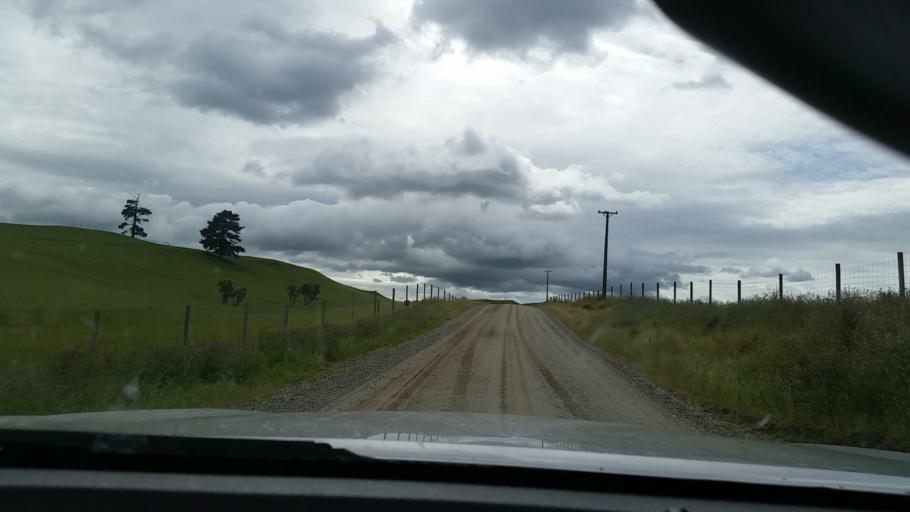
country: NZ
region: Southland
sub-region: Gore District
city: Gore
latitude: -46.2598
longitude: 168.9328
